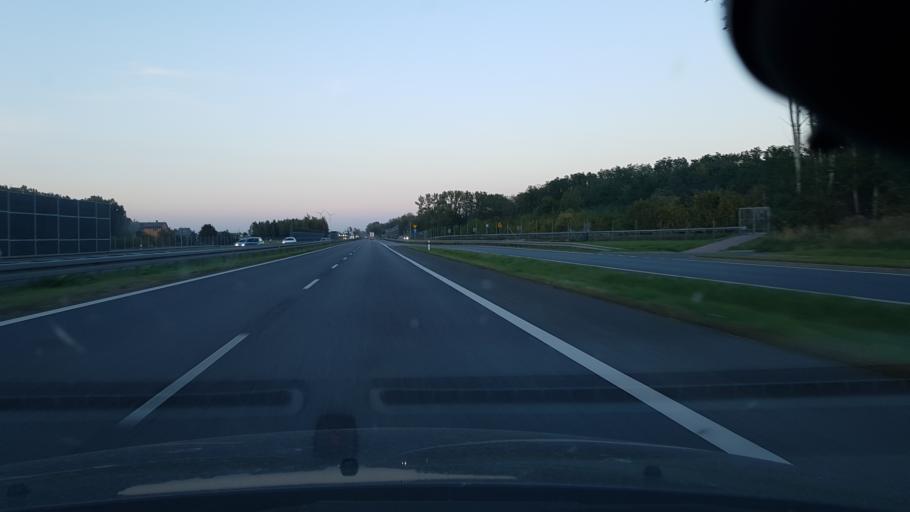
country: PL
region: Masovian Voivodeship
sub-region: Powiat zyrardowski
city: Mszczonow
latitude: 51.9527
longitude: 20.4923
